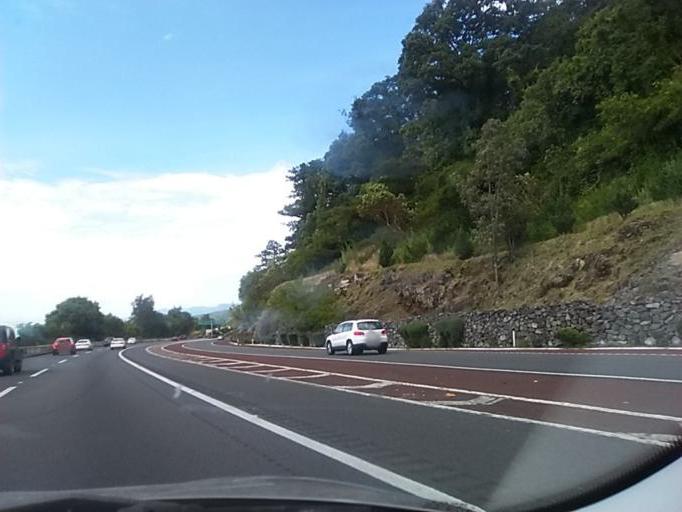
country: MX
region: Morelos
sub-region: Cuernavaca
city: Villa Santiago
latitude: 19.0109
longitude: -99.1685
